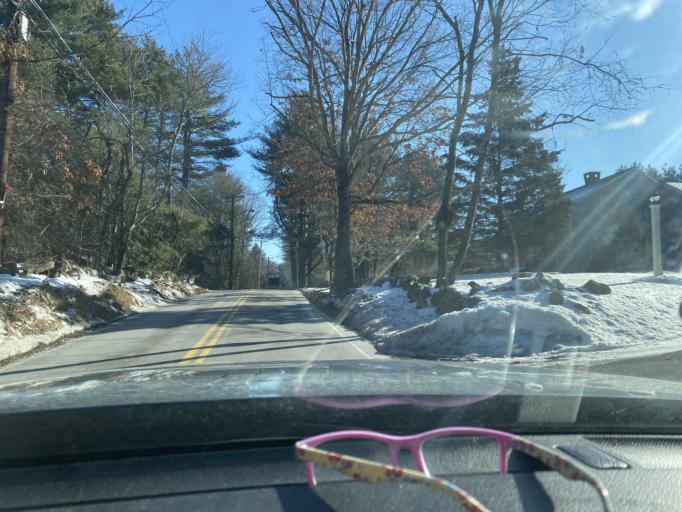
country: US
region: Massachusetts
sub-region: Norfolk County
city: Walpole
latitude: 42.1638
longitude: -71.2578
